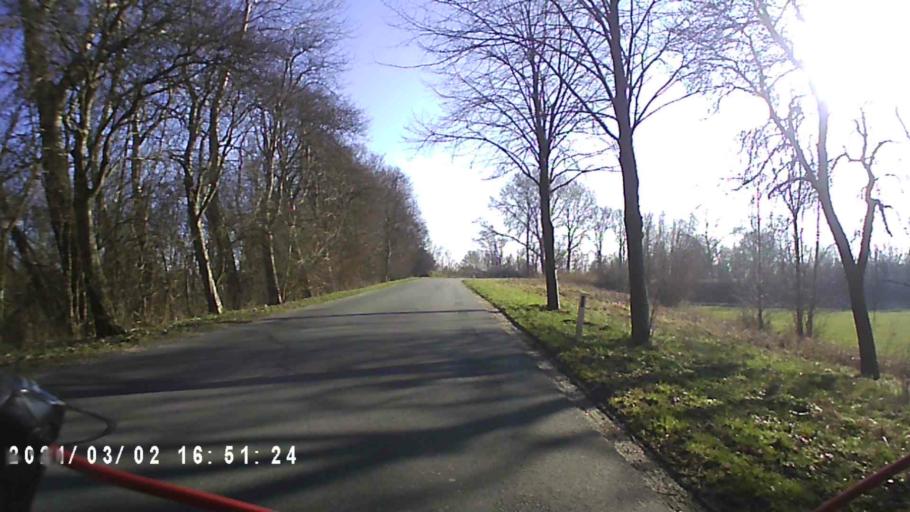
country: NL
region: Groningen
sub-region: Gemeente Grootegast
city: Grootegast
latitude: 53.2440
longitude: 6.2517
